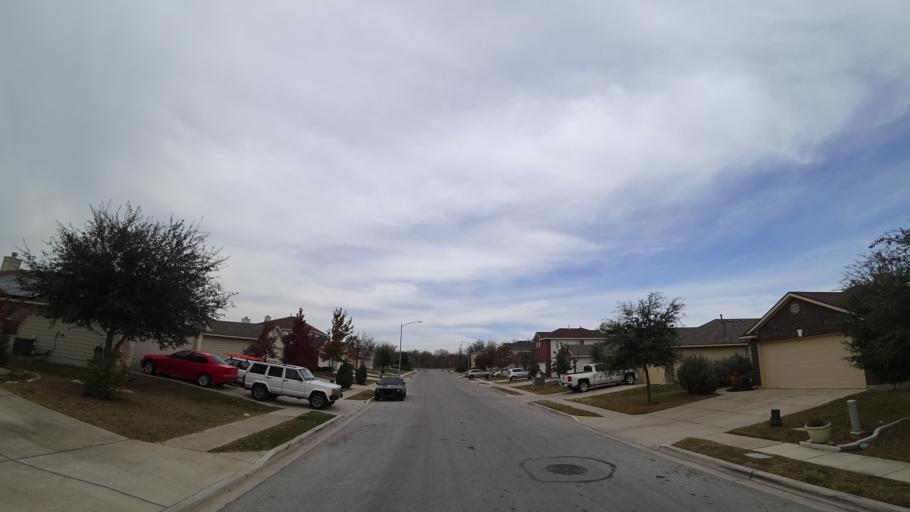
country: US
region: Texas
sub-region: Travis County
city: Onion Creek
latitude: 30.1586
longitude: -97.7502
